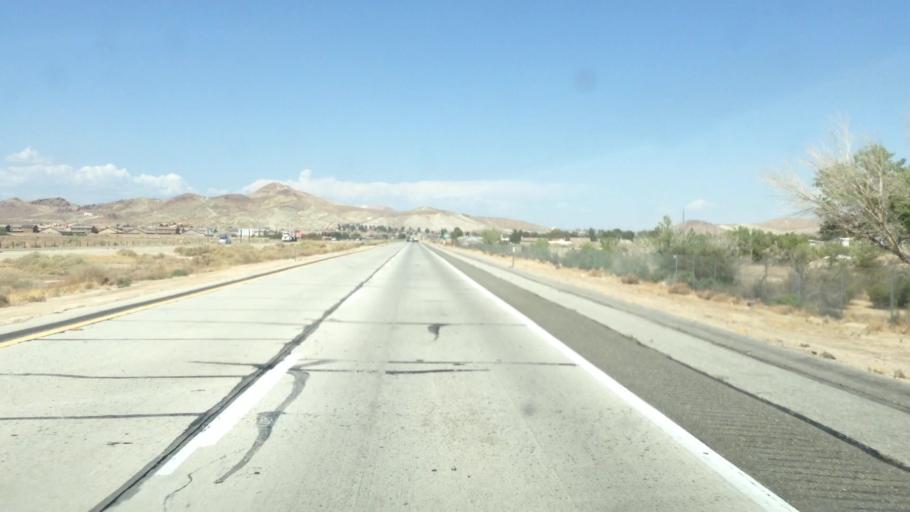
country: US
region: California
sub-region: Kern County
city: Rosamond
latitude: 34.8487
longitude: -118.1699
